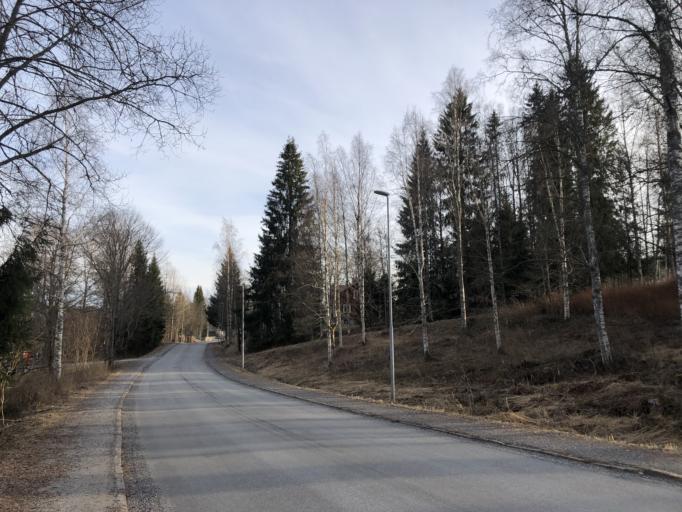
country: SE
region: Vaermland
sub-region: Filipstads Kommun
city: Lesjofors
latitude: 59.9778
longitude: 14.1795
